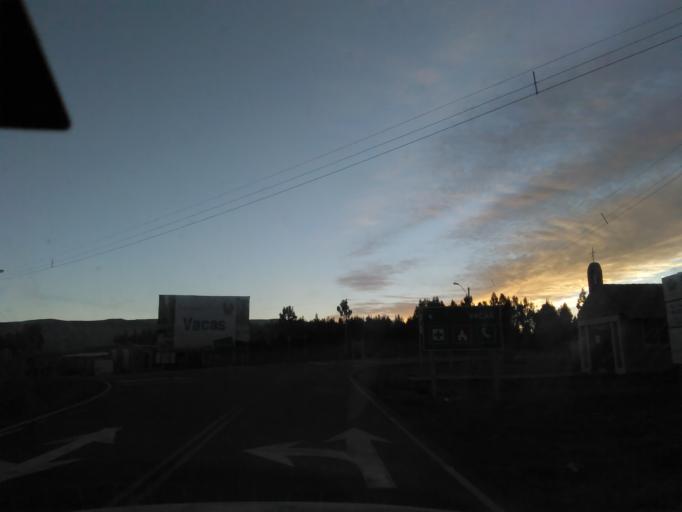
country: BO
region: Cochabamba
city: Arani
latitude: -17.5472
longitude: -65.6729
